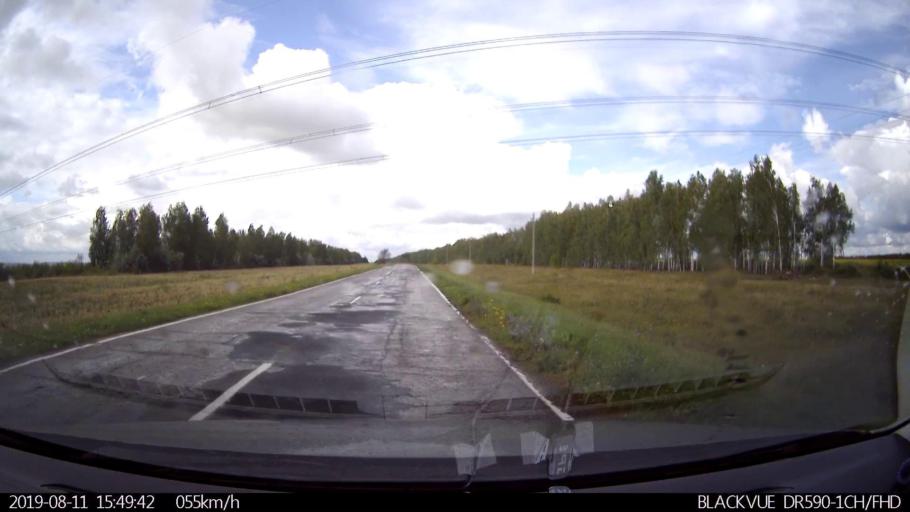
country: RU
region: Ulyanovsk
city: Ignatovka
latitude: 53.9064
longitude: 47.6553
